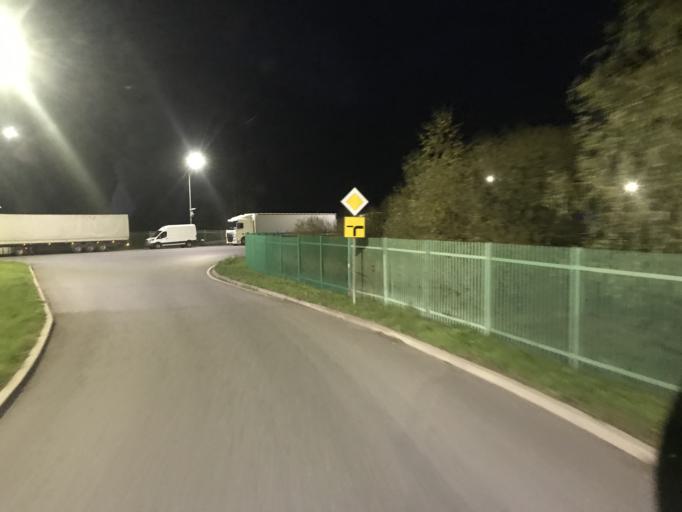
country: PL
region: Lublin Voivodeship
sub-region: Powiat bialski
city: Terespol
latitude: 52.0787
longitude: 23.5233
